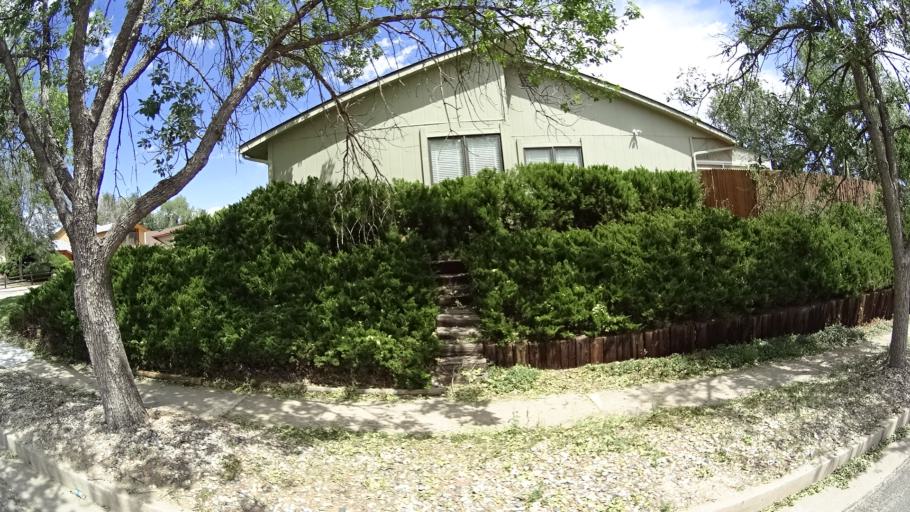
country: US
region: Colorado
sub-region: El Paso County
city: Stratmoor
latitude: 38.7872
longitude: -104.8177
